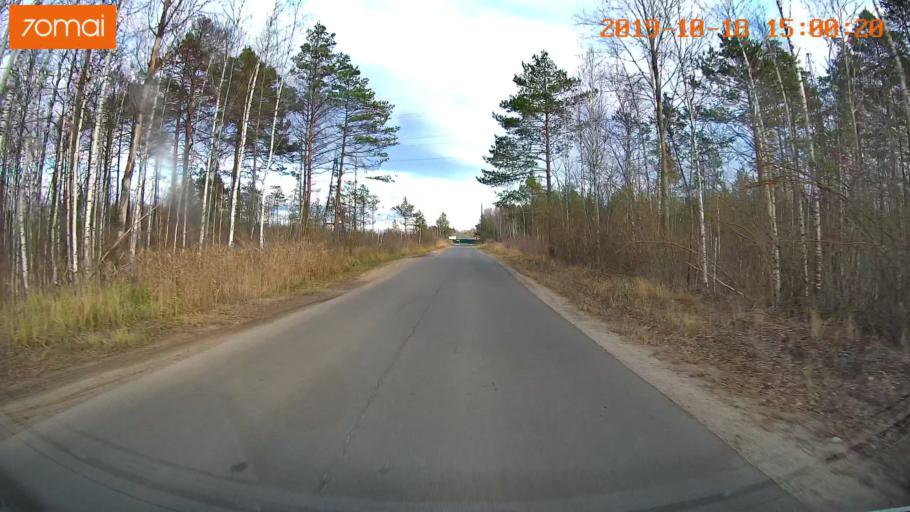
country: RU
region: Vladimir
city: Kurlovo
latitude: 55.4987
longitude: 40.5832
